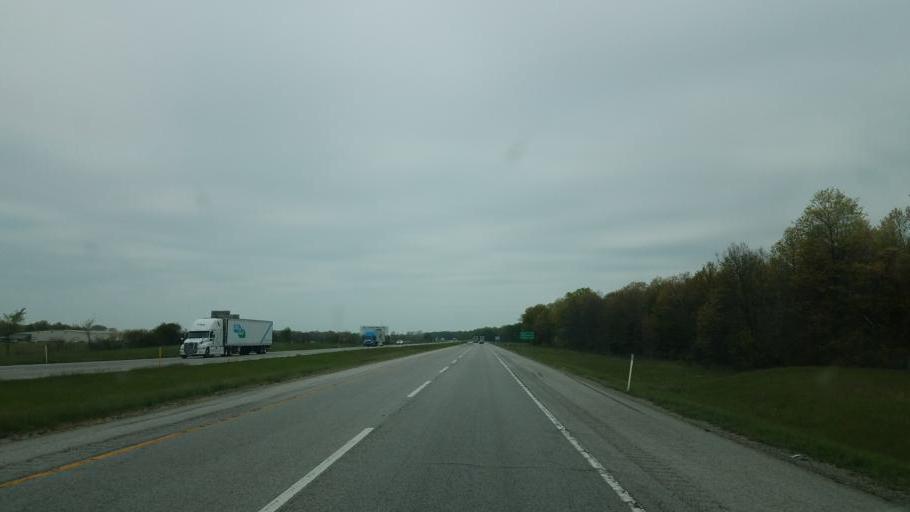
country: US
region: Michigan
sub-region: Saint Joseph County
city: White Pigeon
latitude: 41.7473
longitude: -85.6931
